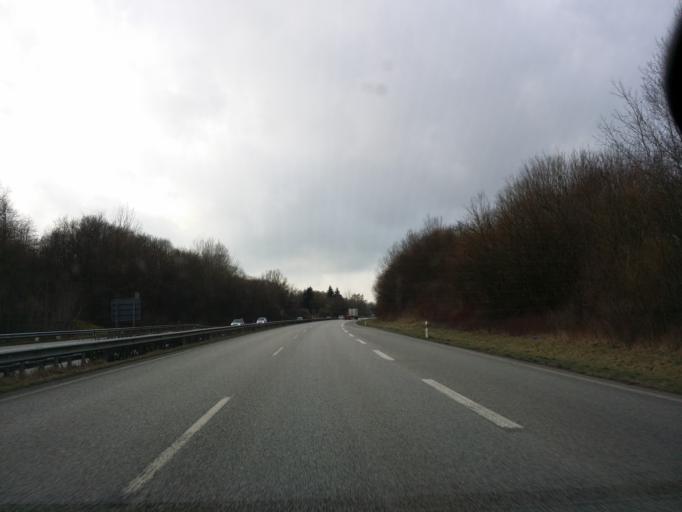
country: DE
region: Schleswig-Holstein
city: Melsdorf
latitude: 54.3066
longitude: 10.0289
